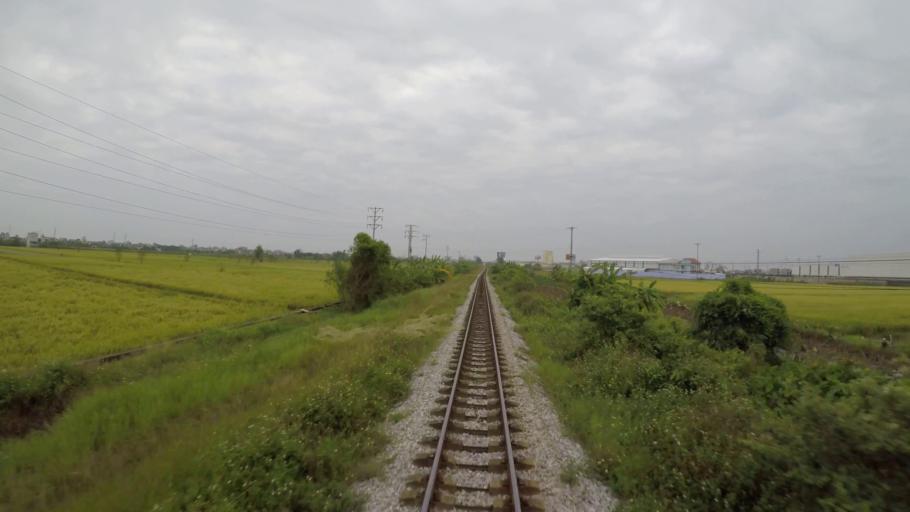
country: VN
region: Hai Duong
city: Lai Cach
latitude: 20.9463
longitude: 106.2658
